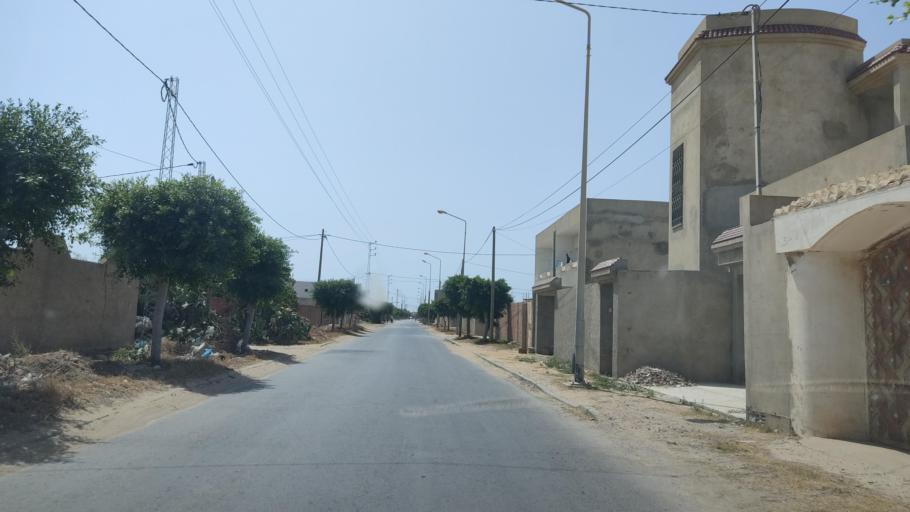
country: TN
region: Safaqis
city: Sfax
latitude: 34.6738
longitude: 10.7018
